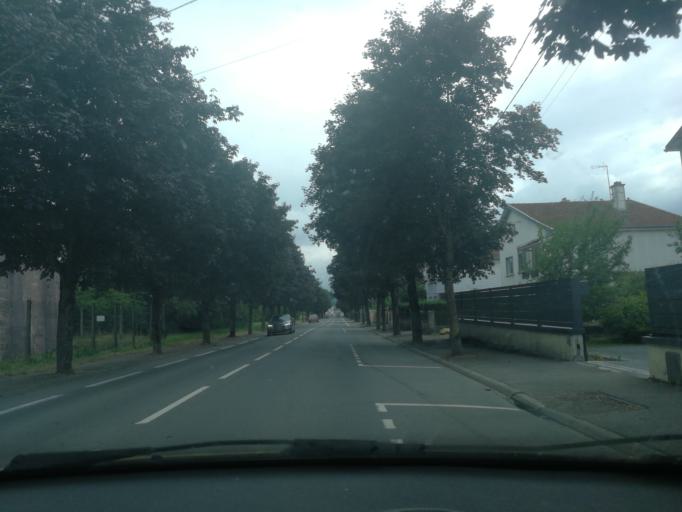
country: FR
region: Lorraine
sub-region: Departement de la Moselle
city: Terville
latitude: 49.3615
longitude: 6.1394
